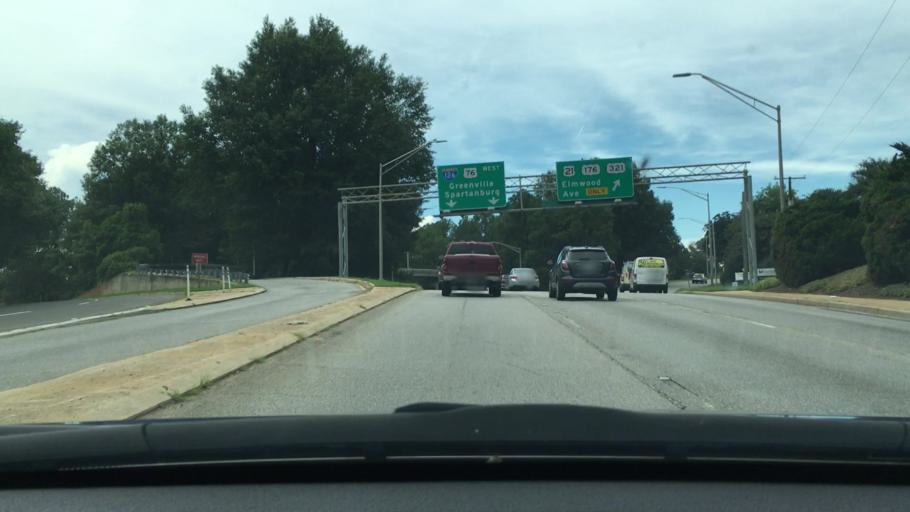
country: US
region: South Carolina
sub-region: Richland County
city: Columbia
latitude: 34.0080
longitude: -81.0494
